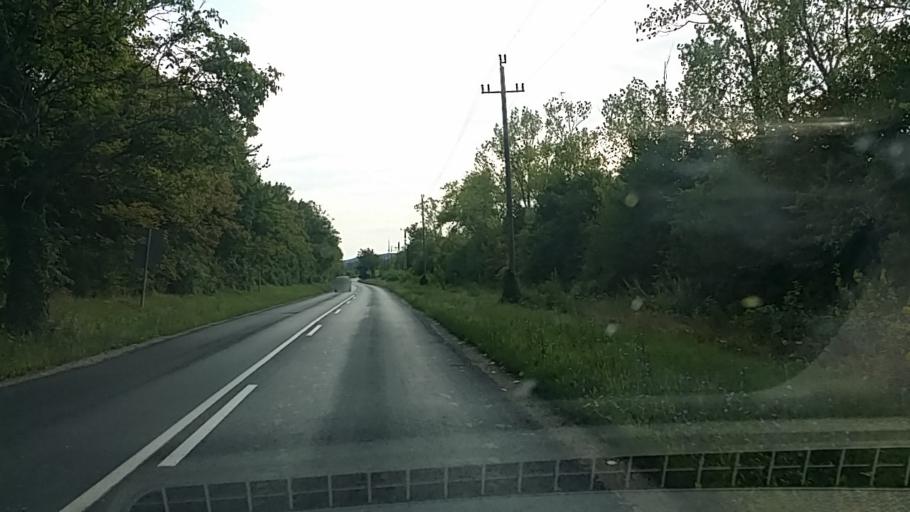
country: HU
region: Gyor-Moson-Sopron
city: Fertorakos
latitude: 47.7182
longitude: 16.6164
